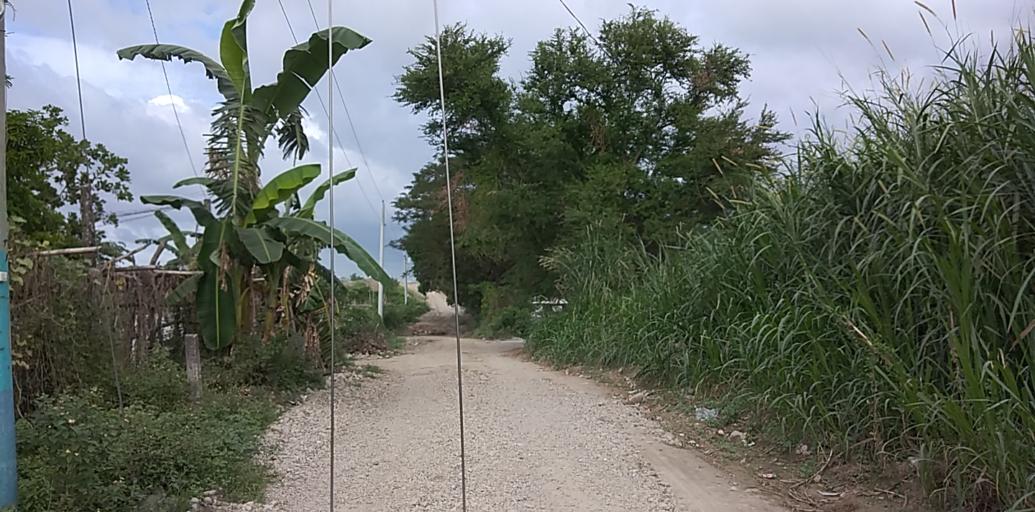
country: PH
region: Central Luzon
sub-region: Province of Pampanga
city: Pulung Santol
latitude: 15.0585
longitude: 120.5658
